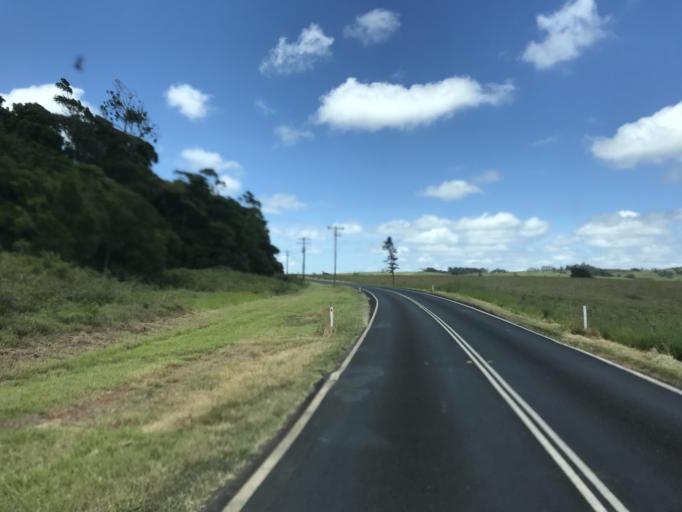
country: AU
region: Queensland
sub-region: Tablelands
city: Ravenshoe
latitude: -17.4967
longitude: 145.4768
